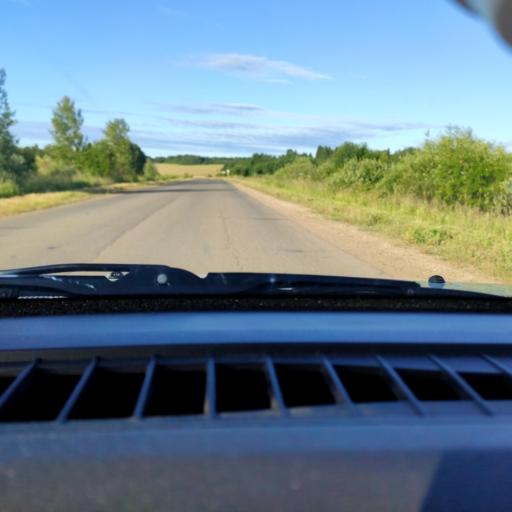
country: RU
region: Perm
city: Uinskoye
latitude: 57.0840
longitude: 56.5564
